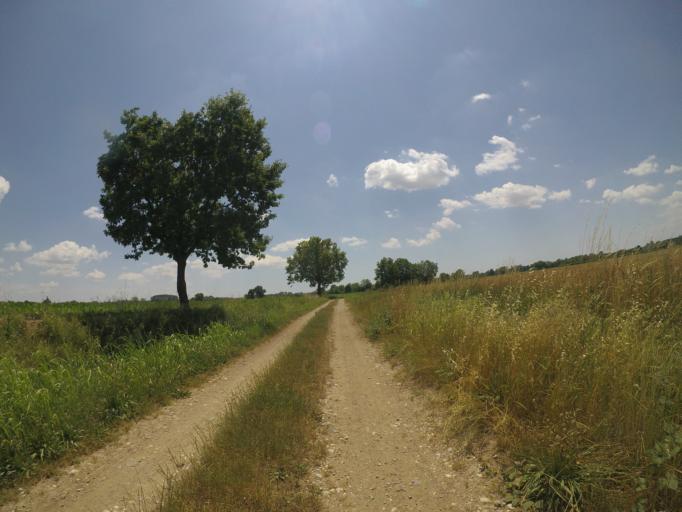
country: IT
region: Friuli Venezia Giulia
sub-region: Provincia di Udine
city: Bertiolo
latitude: 45.9358
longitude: 13.0641
